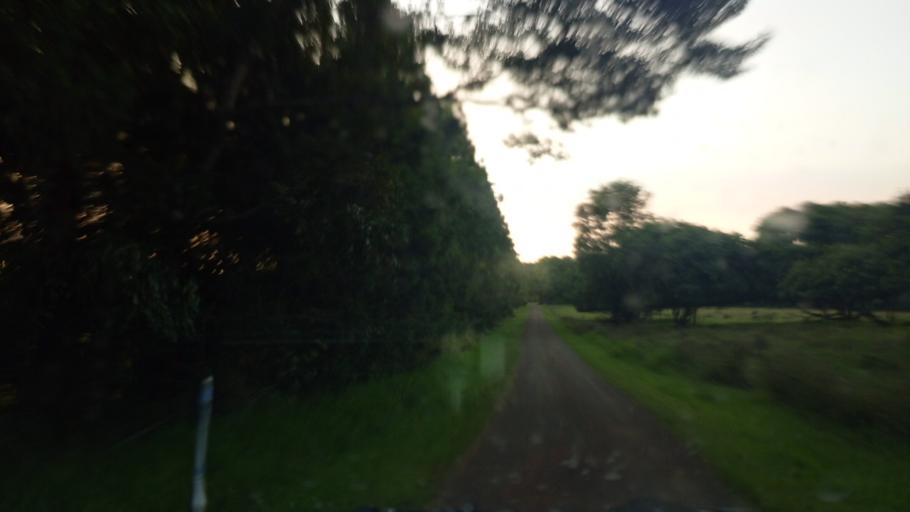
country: AU
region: Queensland
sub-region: Tablelands
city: Atherton
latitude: -17.3671
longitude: 145.7523
